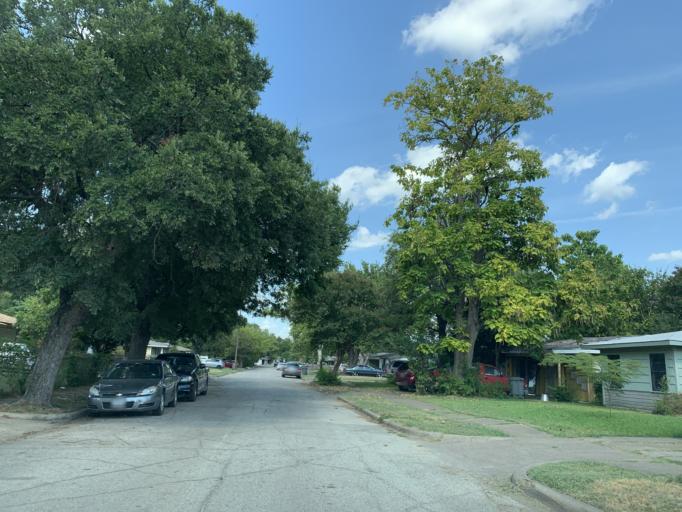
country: US
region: Texas
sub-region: Dallas County
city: Hutchins
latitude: 32.6995
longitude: -96.7736
